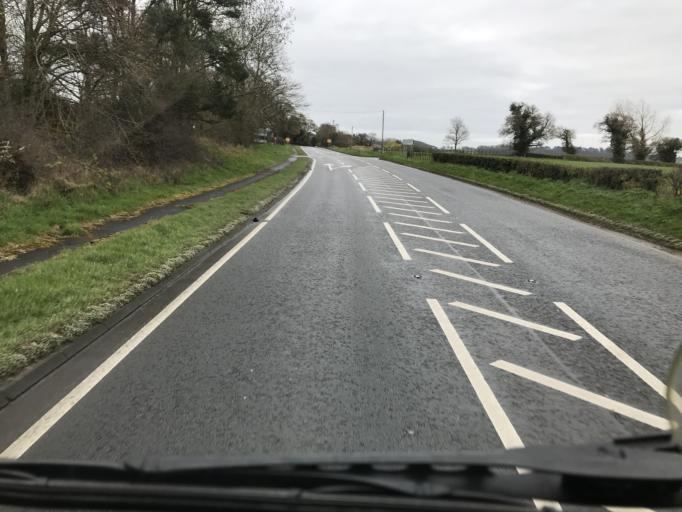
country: GB
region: England
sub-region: Cheshire West and Chester
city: Tattenhall
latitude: 53.1077
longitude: -2.7835
